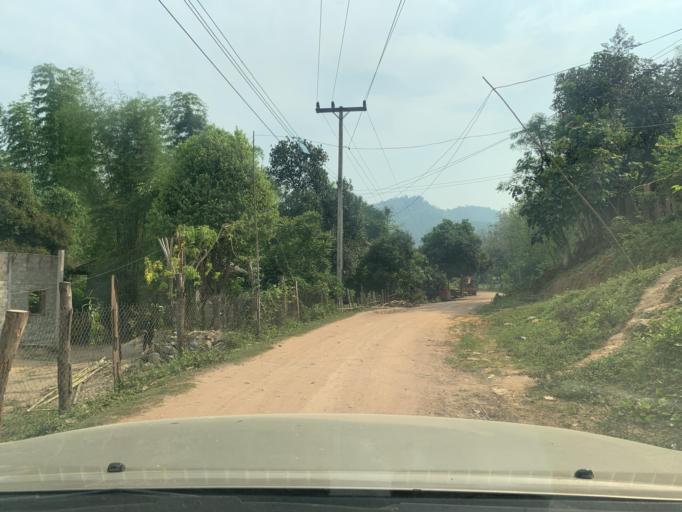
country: LA
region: Louangphabang
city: Louangphabang
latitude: 19.9139
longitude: 102.1383
